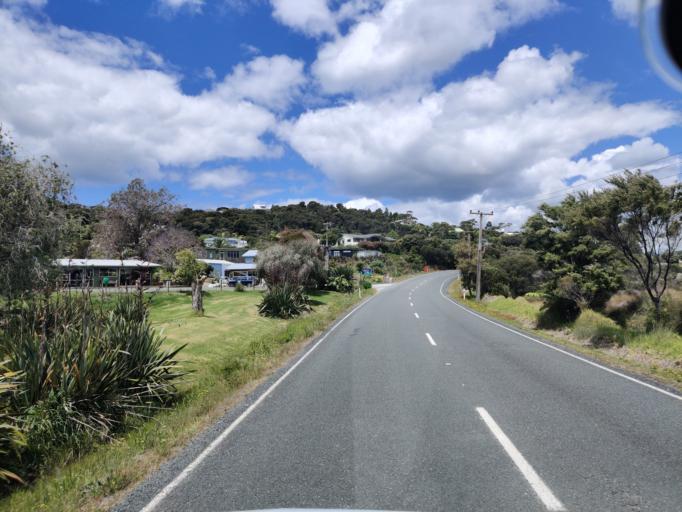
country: NZ
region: Northland
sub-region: Far North District
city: Paihia
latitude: -35.2815
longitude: 174.1466
